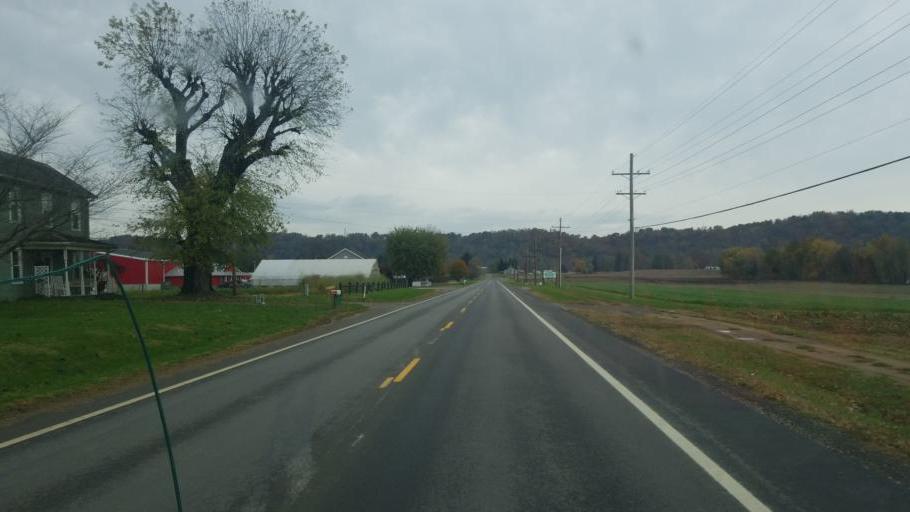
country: US
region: Ohio
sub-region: Washington County
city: Beverly
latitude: 39.5583
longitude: -81.5860
